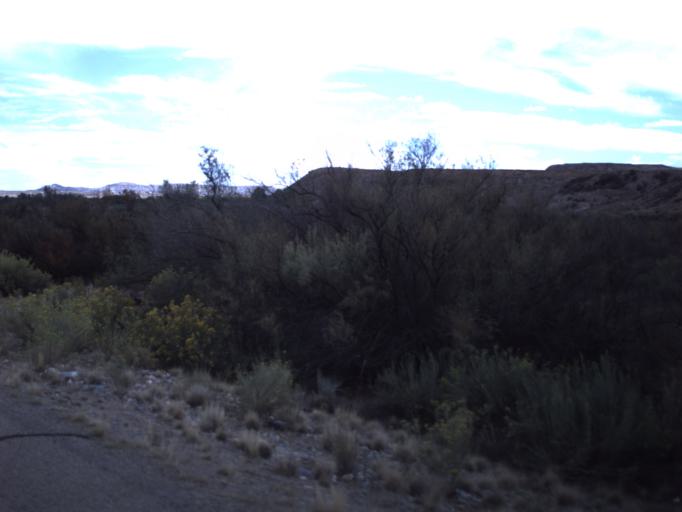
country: US
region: Utah
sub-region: San Juan County
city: Blanding
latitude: 37.2715
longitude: -109.3267
